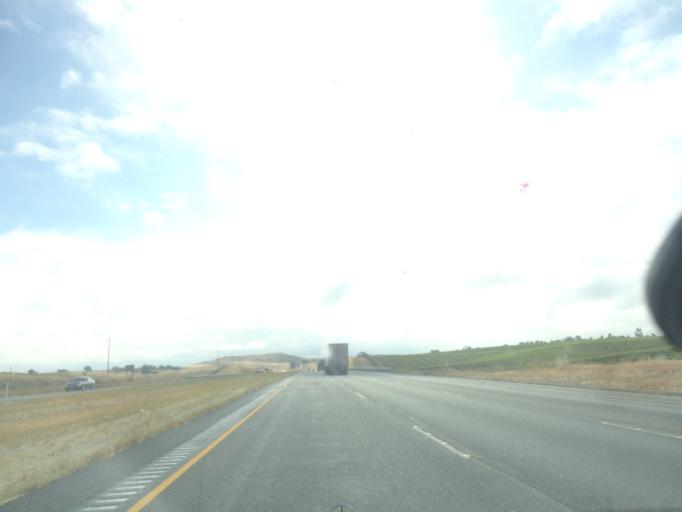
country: US
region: California
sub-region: San Luis Obispo County
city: Paso Robles
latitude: 35.6593
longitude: -120.5582
